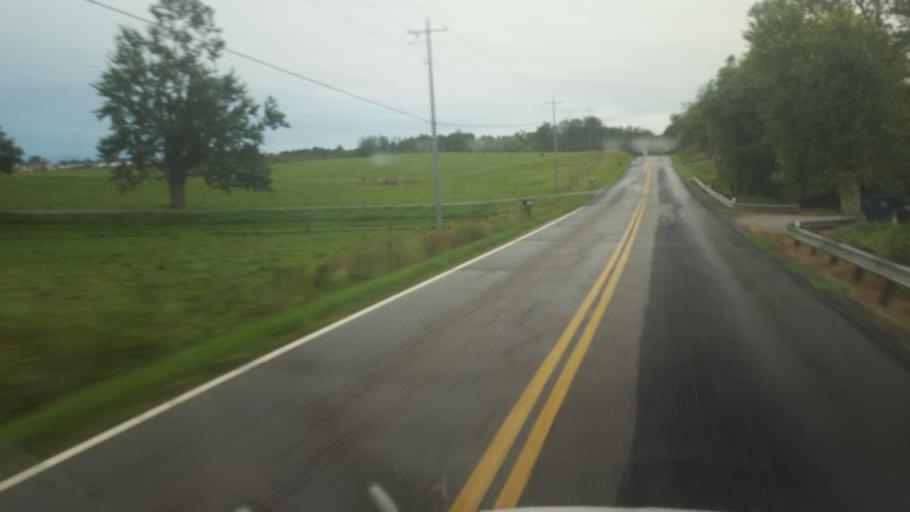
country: US
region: Ohio
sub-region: Licking County
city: Johnstown
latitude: 40.1683
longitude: -82.6909
